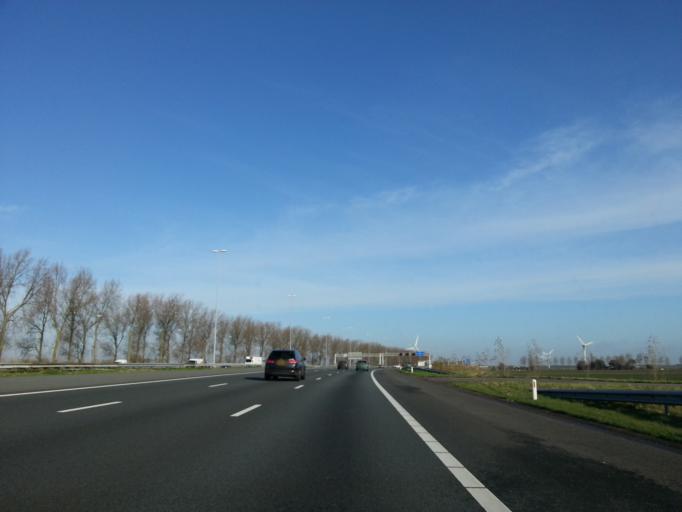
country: NL
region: South Holland
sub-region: Gemeente Kaag en Braassem
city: Oude Wetering
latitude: 52.2194
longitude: 4.6299
